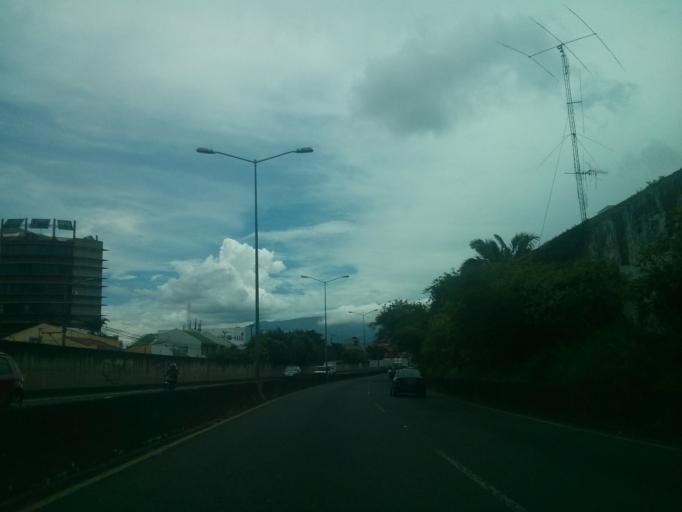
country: CR
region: San Jose
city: San Rafael
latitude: 9.9412
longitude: -84.1171
